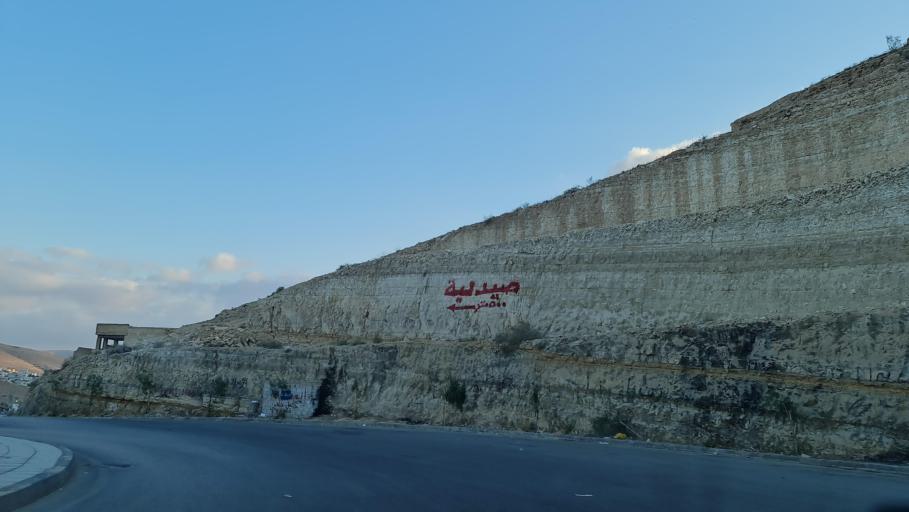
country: JO
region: Zarqa
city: Zarqa
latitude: 32.0818
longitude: 36.0691
